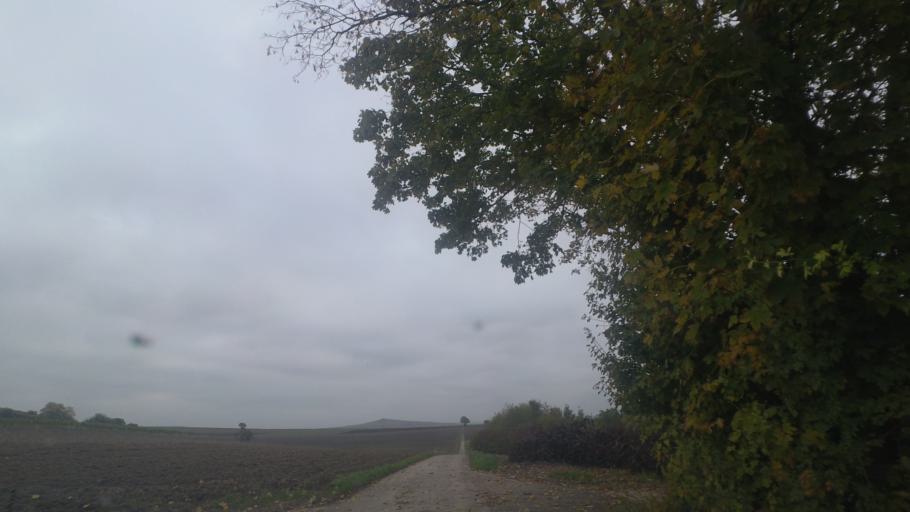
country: DE
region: Rheinland-Pfalz
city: Weinolsheim
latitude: 49.8135
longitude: 8.2542
